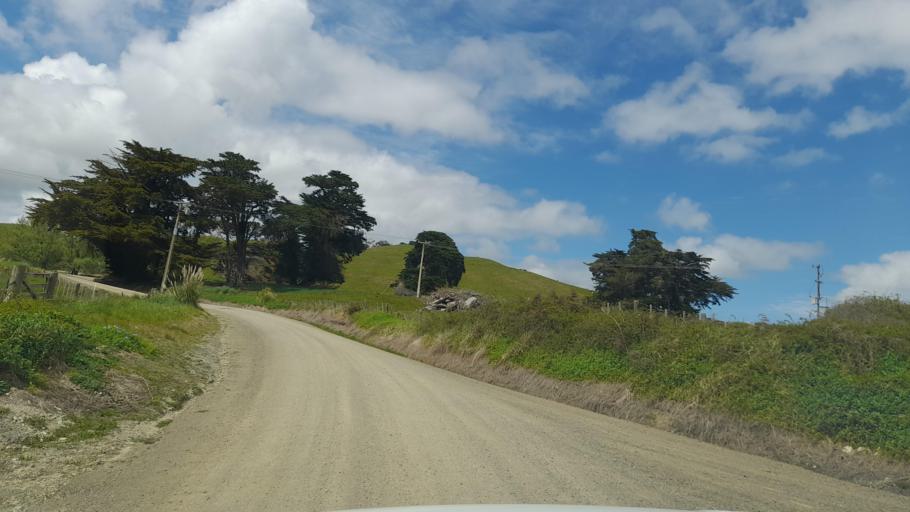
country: NZ
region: Auckland
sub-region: Auckland
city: Wellsford
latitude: -36.1811
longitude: 174.3156
